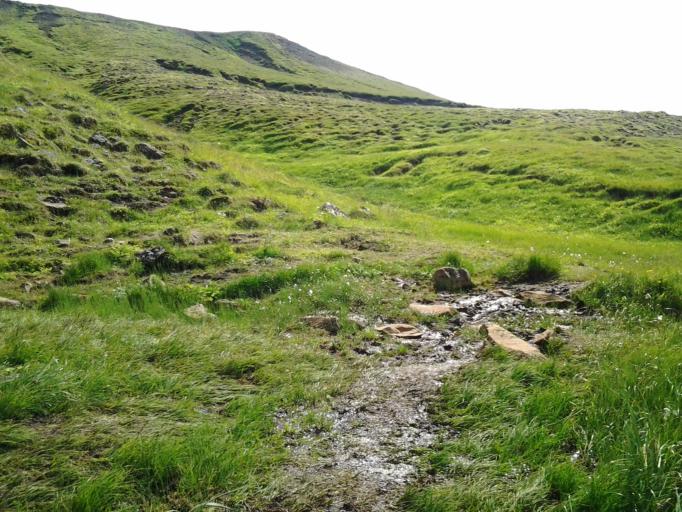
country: IS
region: South
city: Hveragerdi
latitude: 64.0446
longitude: -21.2182
